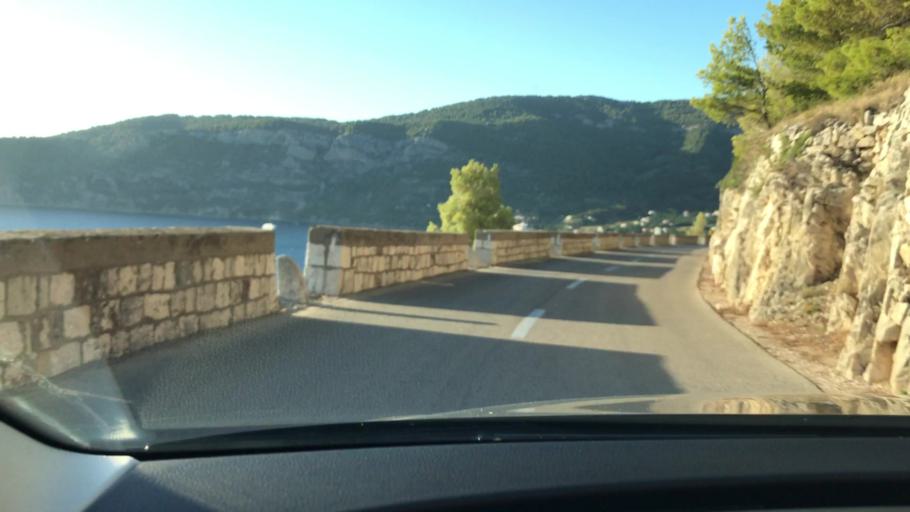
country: HR
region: Splitsko-Dalmatinska
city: Komiza
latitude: 43.0328
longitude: 16.0948
